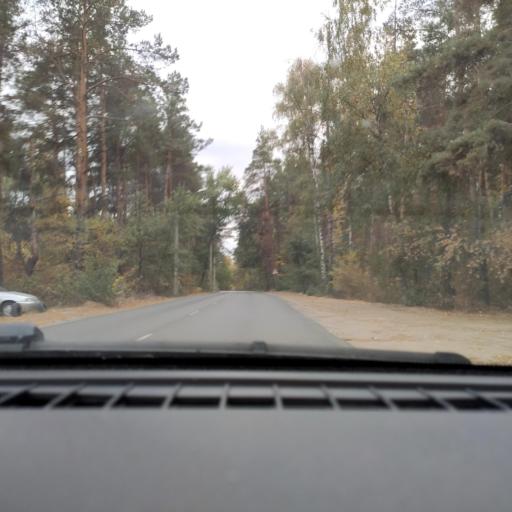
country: RU
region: Voronezj
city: Voronezh
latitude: 51.6860
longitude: 39.2783
